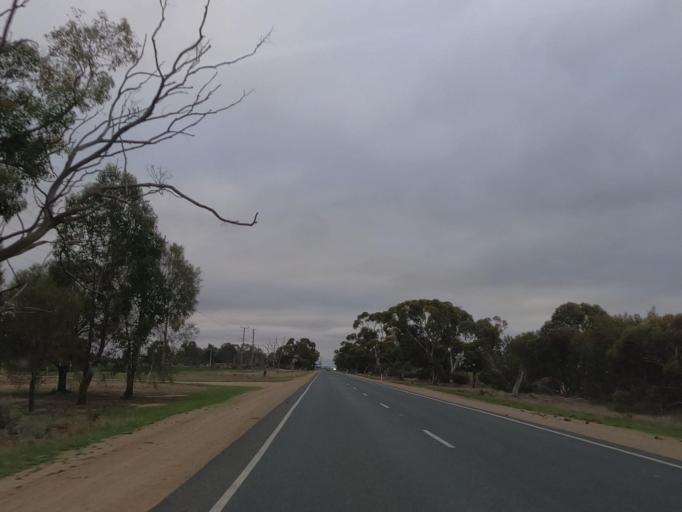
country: AU
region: Victoria
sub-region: Swan Hill
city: Swan Hill
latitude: -35.3996
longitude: 143.5762
